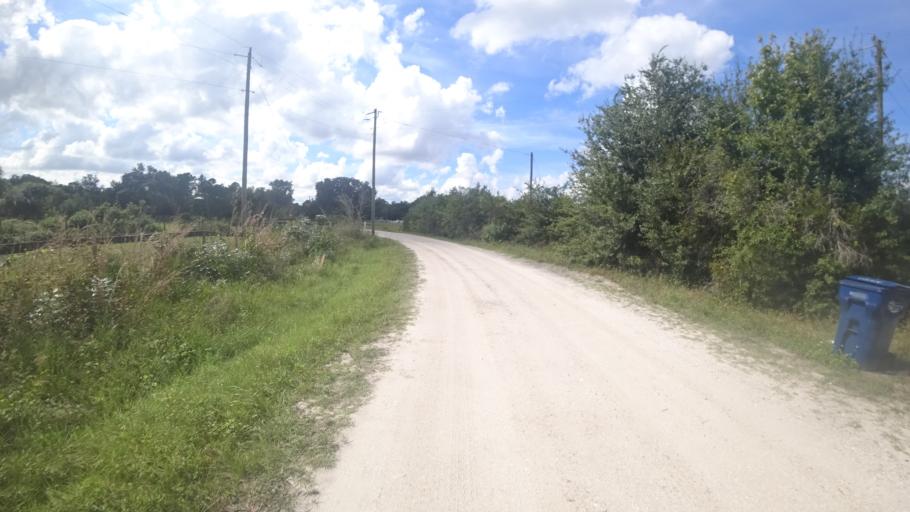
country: US
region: Florida
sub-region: Hillsborough County
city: Sun City Center
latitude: 27.6465
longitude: -82.3771
